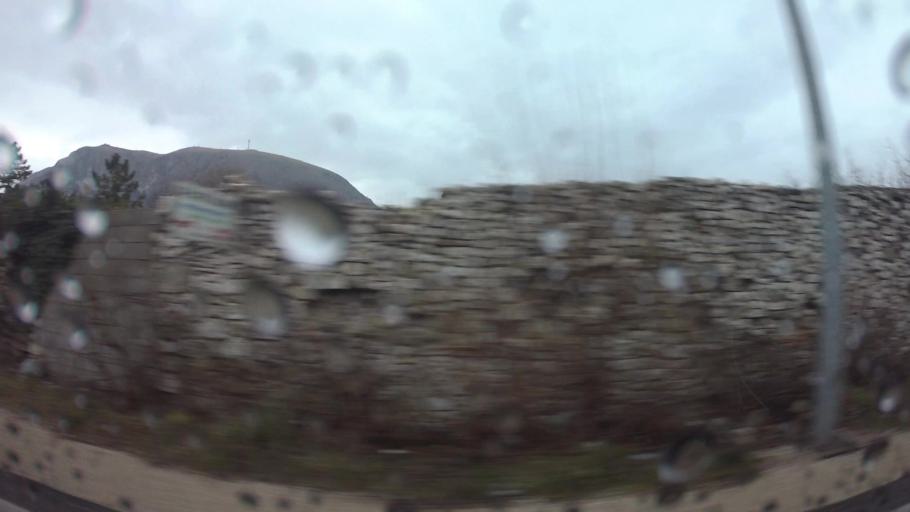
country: BA
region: Federation of Bosnia and Herzegovina
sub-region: Hercegovacko-Bosanski Kanton
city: Mostar
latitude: 43.3374
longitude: 17.8182
